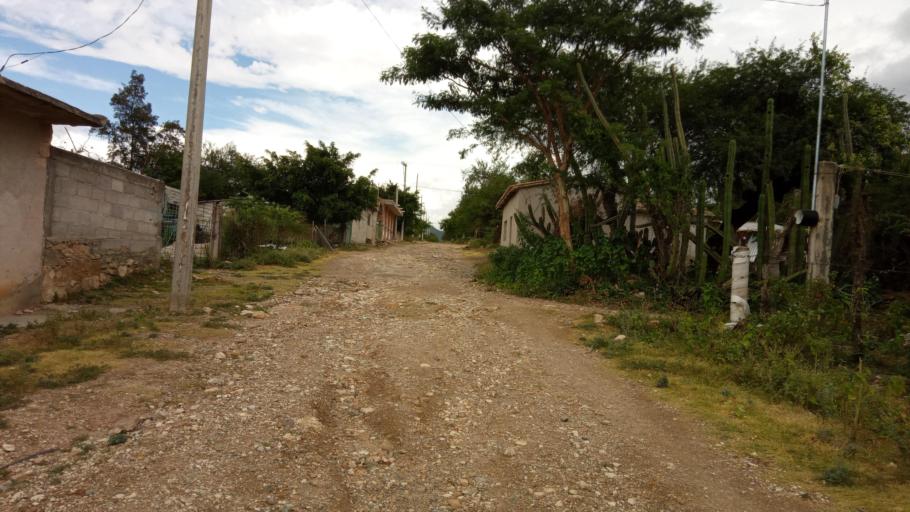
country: MX
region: Puebla
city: Totoltepec de Guerrero
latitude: 18.2958
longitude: -97.7752
